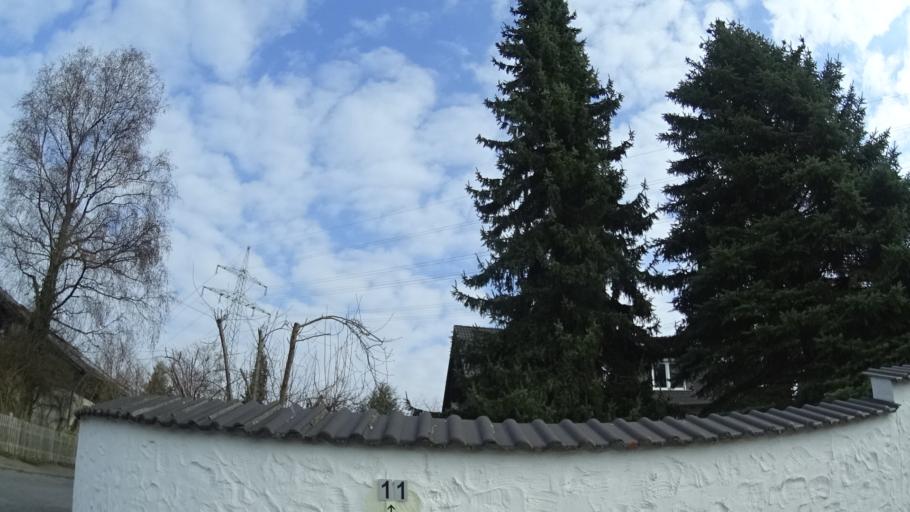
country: DE
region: Bavaria
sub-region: Regierungsbezirk Mittelfranken
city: Winkelhaid
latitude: 49.4118
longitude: 11.2983
